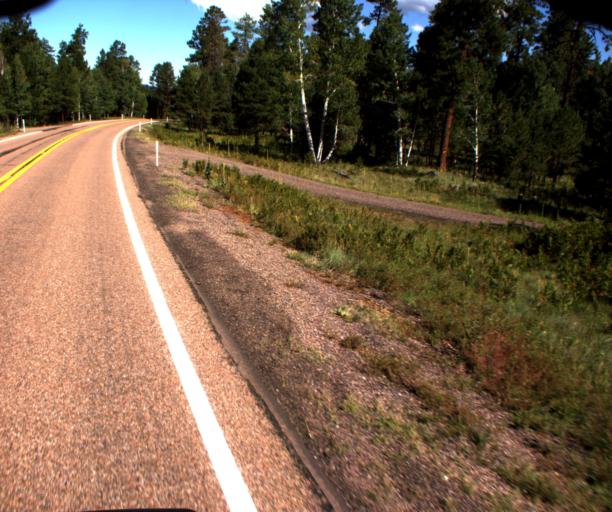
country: US
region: Arizona
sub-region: Navajo County
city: Pinetop-Lakeside
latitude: 34.0283
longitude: -109.6579
